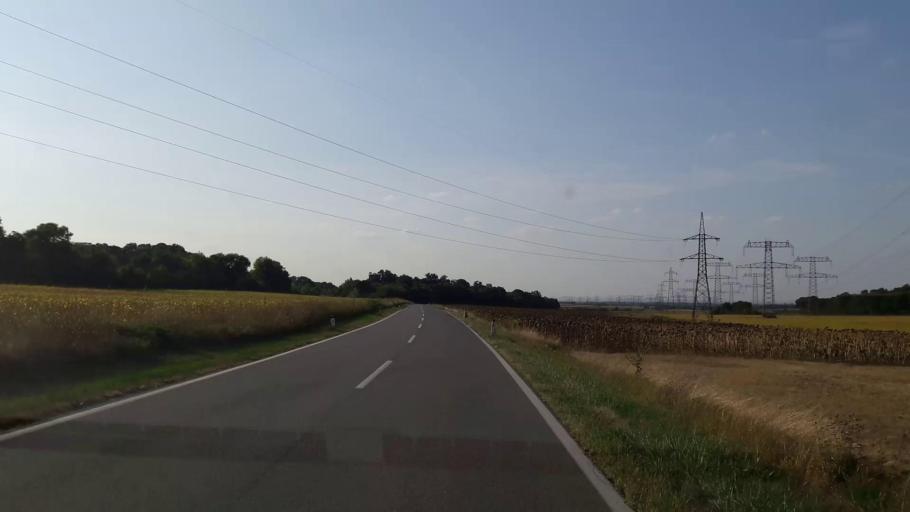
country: AT
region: Lower Austria
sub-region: Politischer Bezirk Ganserndorf
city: Orth an der Donau
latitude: 48.0835
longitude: 16.6756
